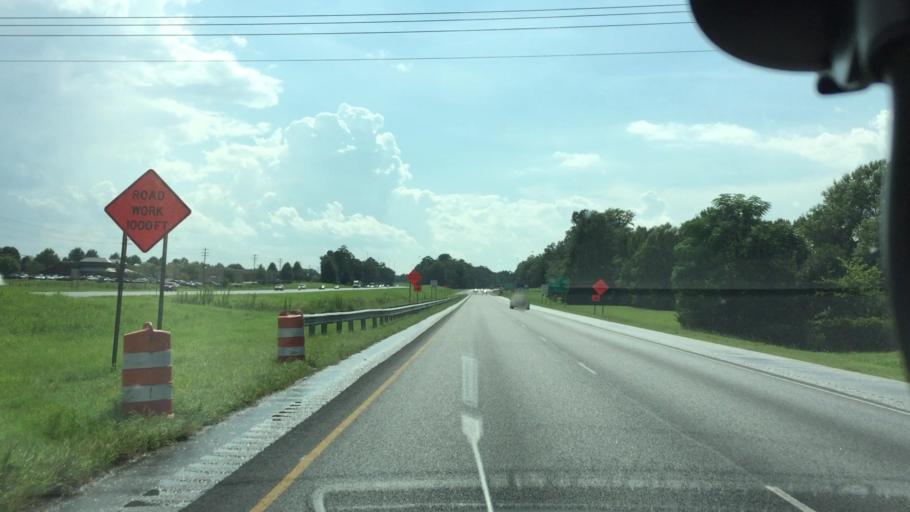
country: US
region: Alabama
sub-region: Montgomery County
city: Pike Road
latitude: 32.3640
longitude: -86.1577
